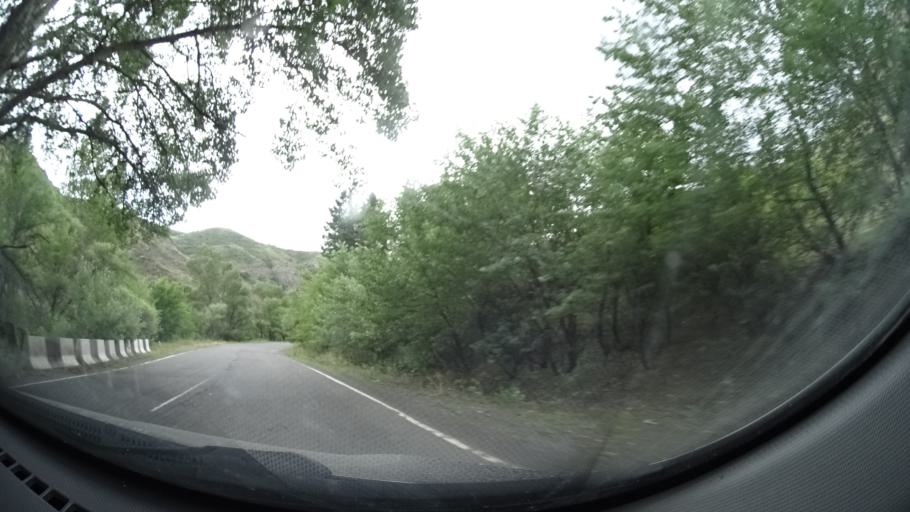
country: GE
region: Samtskhe-Javakheti
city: Akhaltsikhe
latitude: 41.6149
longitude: 43.1002
